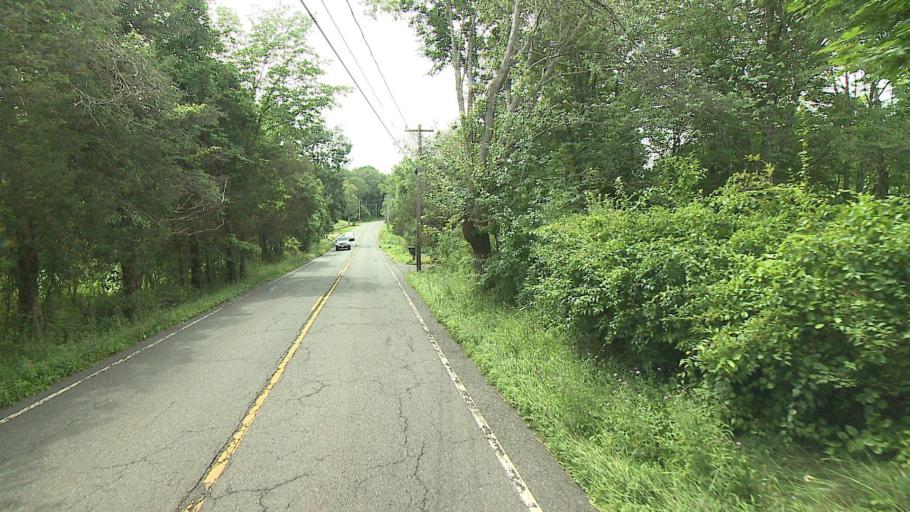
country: US
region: Connecticut
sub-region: Litchfield County
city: New Milford
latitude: 41.5108
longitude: -73.3600
